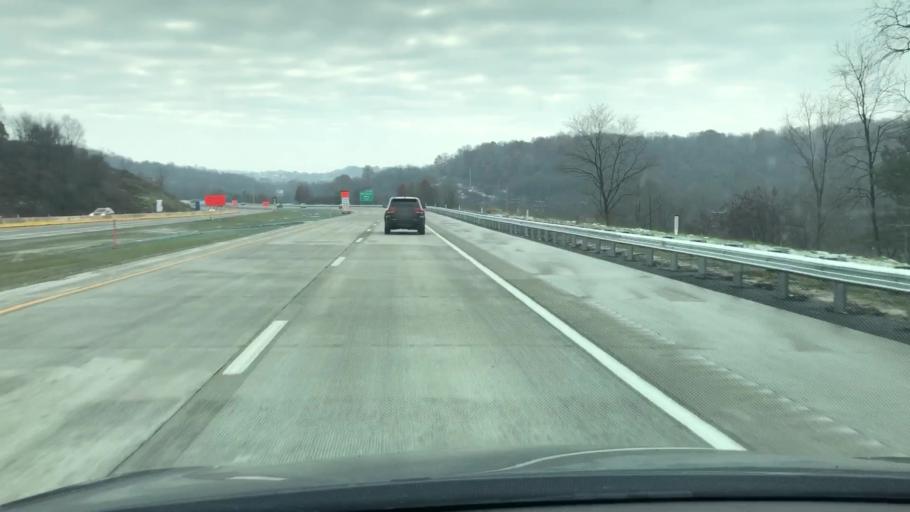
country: US
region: Pennsylvania
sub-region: Allegheny County
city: Imperial
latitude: 40.4710
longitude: -80.2473
